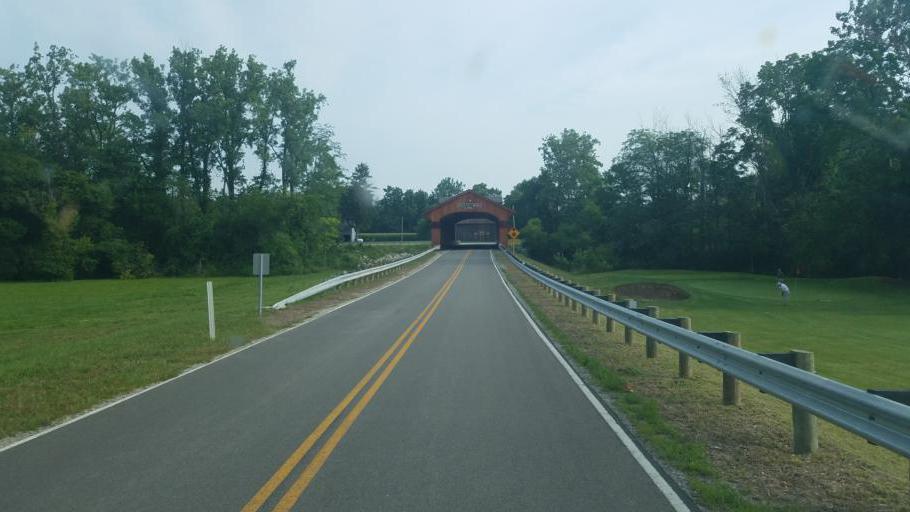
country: US
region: Ohio
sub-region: Marion County
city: Marion
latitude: 40.5112
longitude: -83.0533
